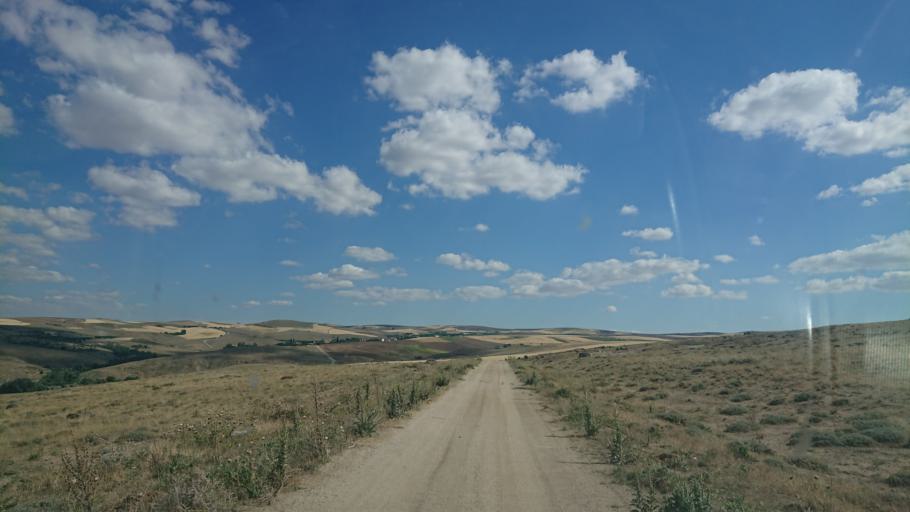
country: TR
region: Aksaray
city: Sariyahsi
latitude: 38.9252
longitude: 33.8526
